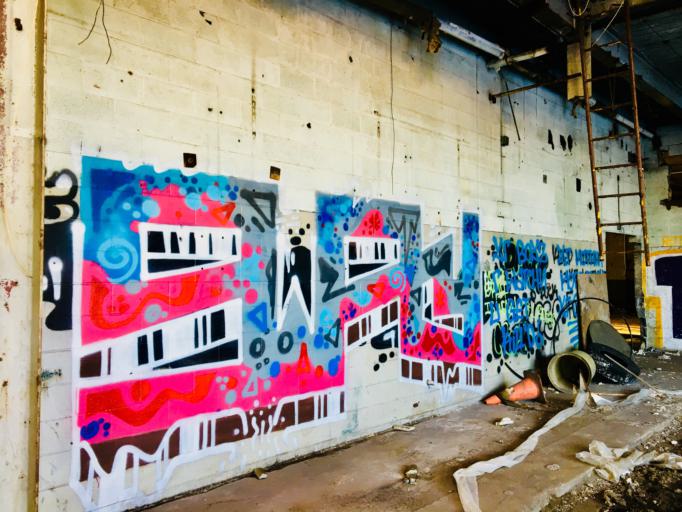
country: US
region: Michigan
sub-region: Wayne County
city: Hamtramck
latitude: 42.4237
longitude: -83.0364
